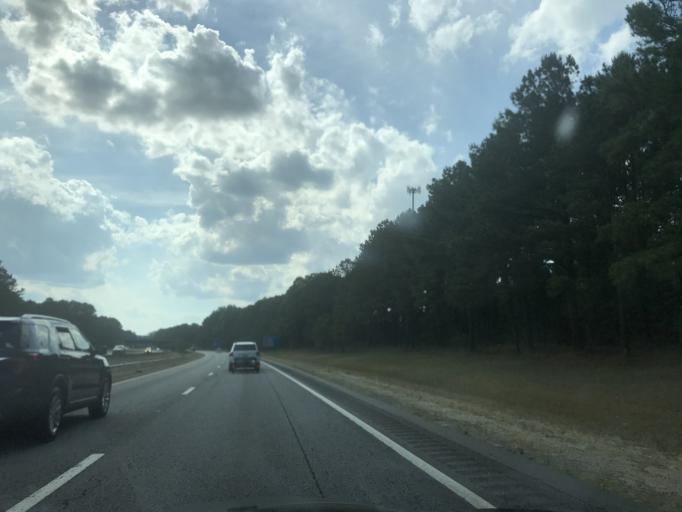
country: US
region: North Carolina
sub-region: Nash County
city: Rocky Mount
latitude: 35.9703
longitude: -77.8286
